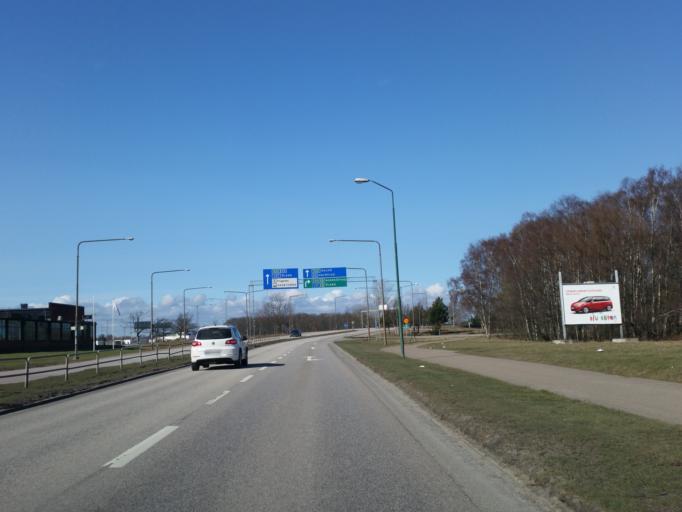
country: SE
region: Kalmar
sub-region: Kalmar Kommun
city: Kalmar
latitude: 56.6730
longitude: 16.3288
